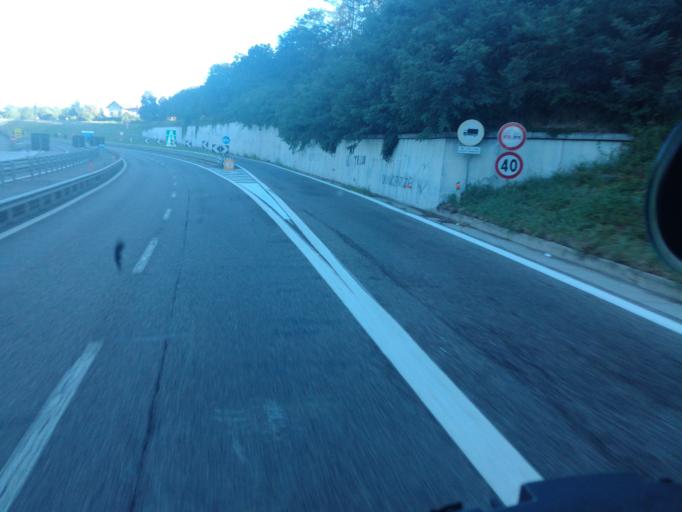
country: IT
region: Lombardy
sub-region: Provincia di Monza e Brianza
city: Barlassina
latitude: 45.6640
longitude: 9.1277
